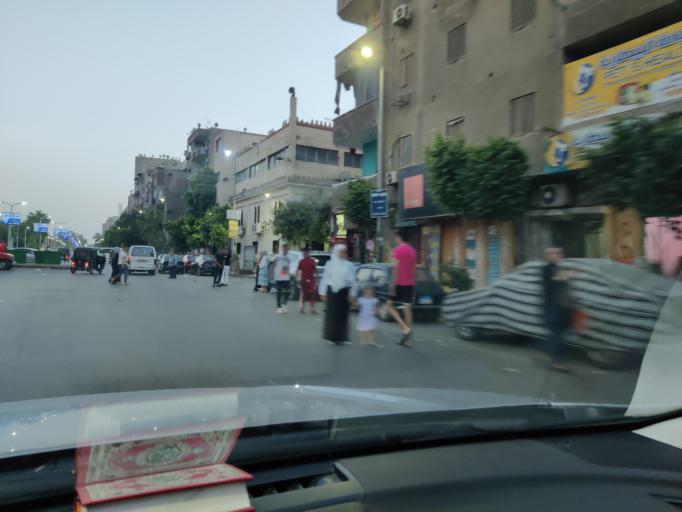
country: EG
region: Muhafazat al Qahirah
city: Cairo
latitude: 30.1079
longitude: 31.3034
